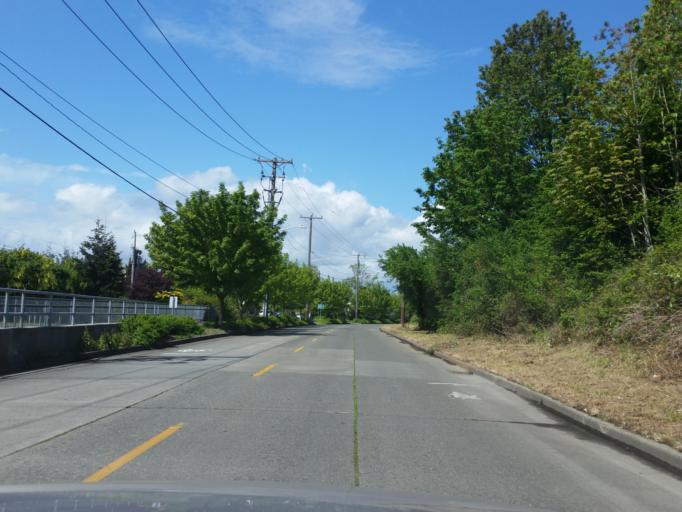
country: US
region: Washington
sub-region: King County
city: Seattle
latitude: 47.6685
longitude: -122.4027
